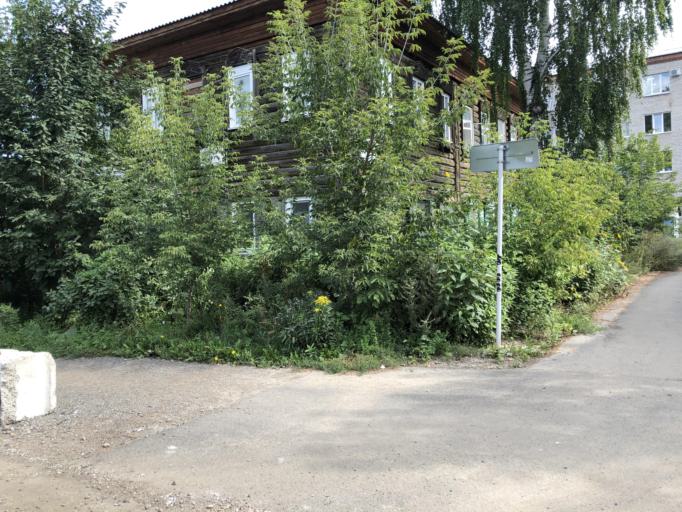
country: RU
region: Tomsk
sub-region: Tomskiy Rayon
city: Tomsk
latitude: 56.4800
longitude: 84.9622
